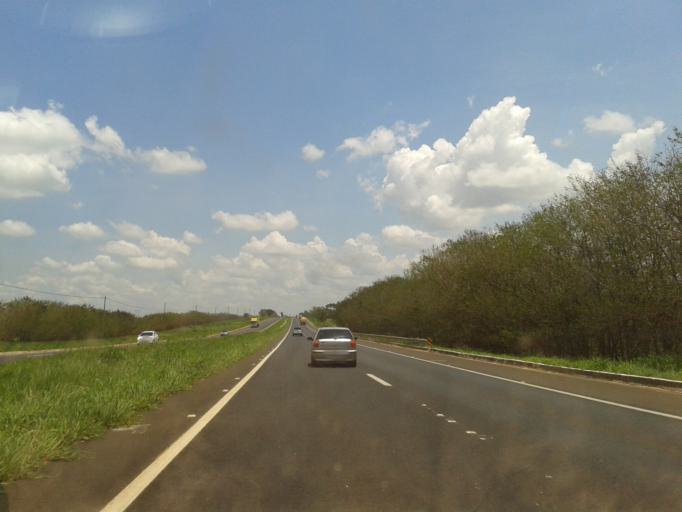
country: BR
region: Minas Gerais
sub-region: Uberlandia
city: Uberlandia
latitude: -18.8787
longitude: -48.5061
